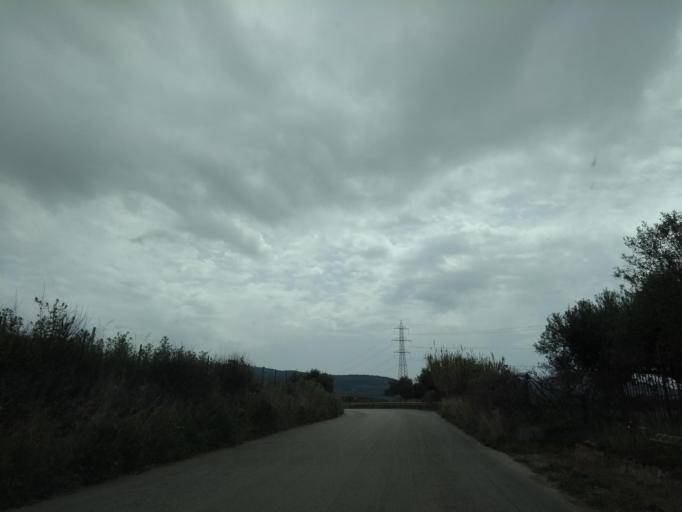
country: IT
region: Sicily
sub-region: Palermo
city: Partinico
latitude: 37.9944
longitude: 13.0658
